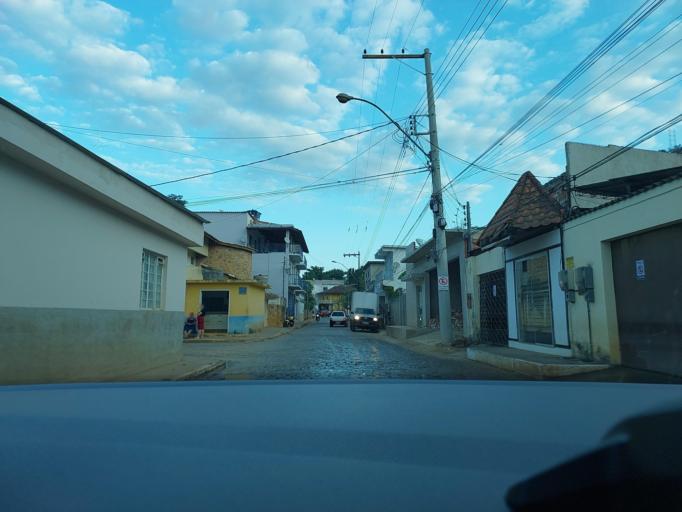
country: BR
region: Rio de Janeiro
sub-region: Natividade
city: Natividade
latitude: -21.1805
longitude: -42.1044
